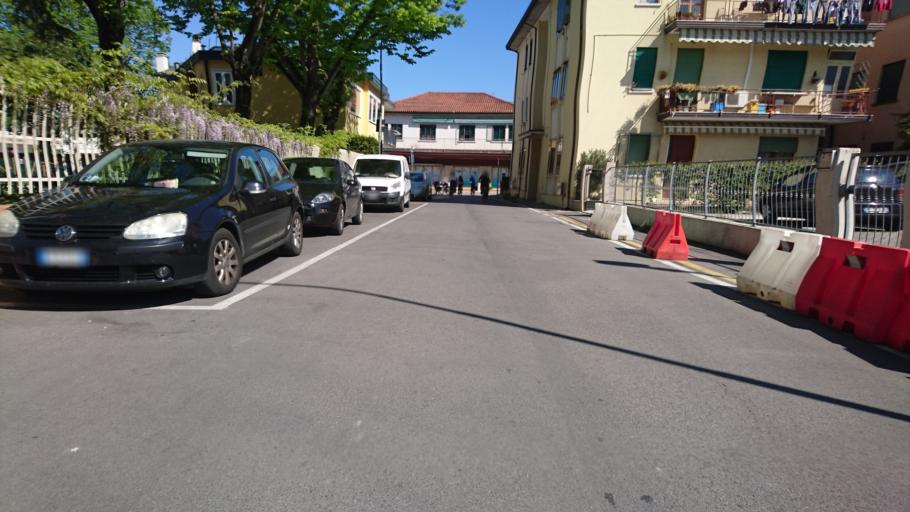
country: IT
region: Veneto
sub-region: Provincia di Venezia
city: Iesolo
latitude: 45.5373
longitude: 12.6396
